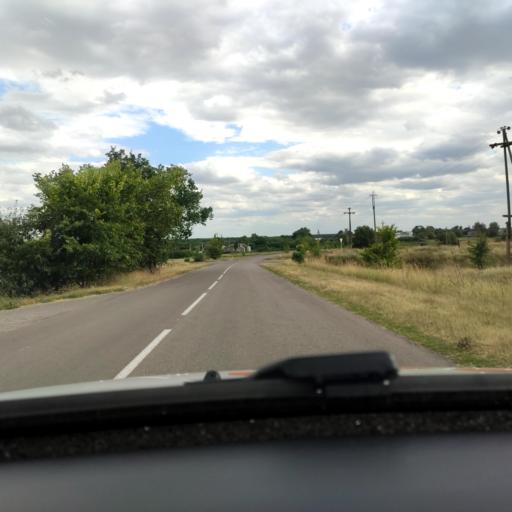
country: RU
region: Voronezj
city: Orlovo
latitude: 51.6661
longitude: 39.5739
